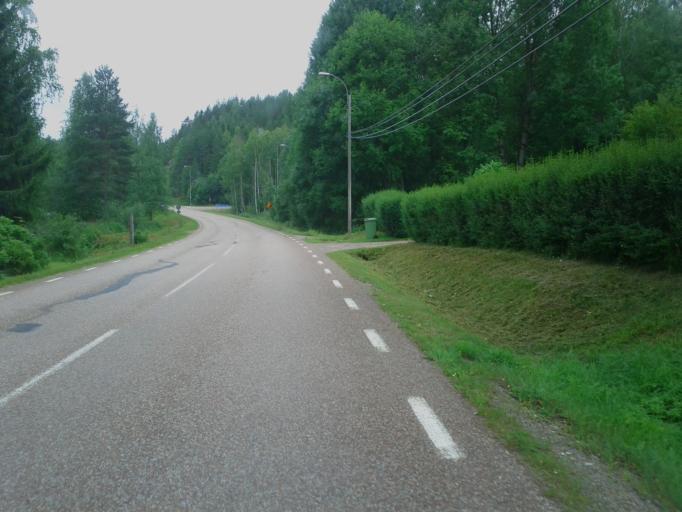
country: SE
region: Dalarna
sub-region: Borlange Kommun
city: Borlaenge
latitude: 60.3198
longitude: 15.3764
